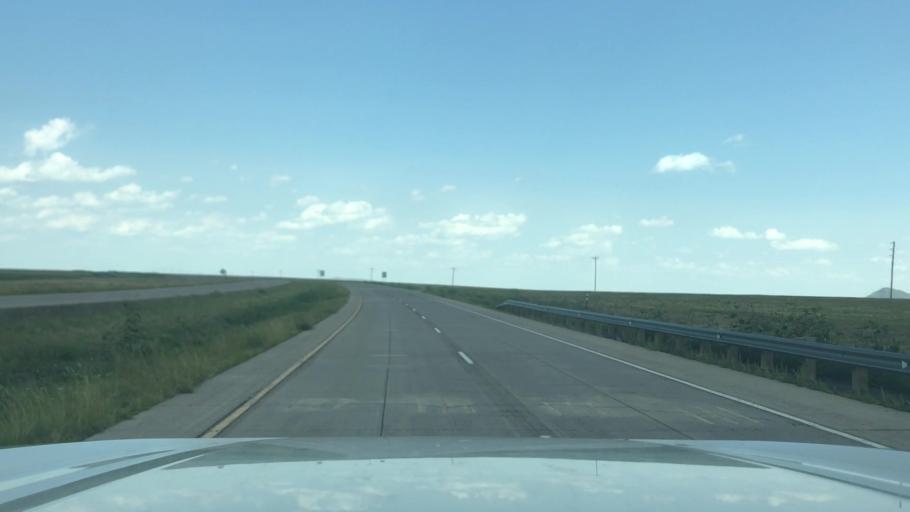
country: US
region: New Mexico
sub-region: Union County
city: Clayton
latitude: 36.6146
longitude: -103.6848
